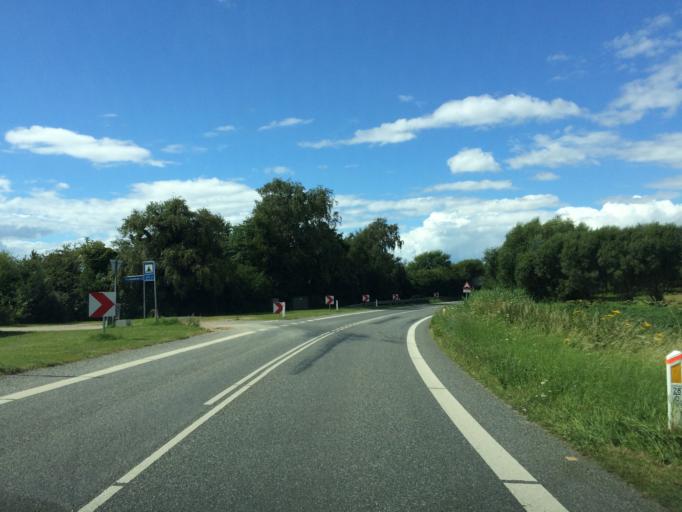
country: DK
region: South Denmark
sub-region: Assens Kommune
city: Harby
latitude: 55.1393
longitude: 10.1657
